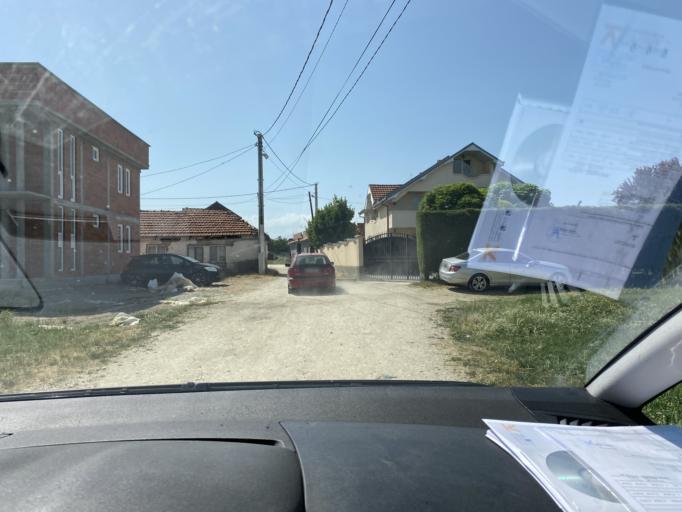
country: MK
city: Creshevo
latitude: 42.0217
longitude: 21.5059
